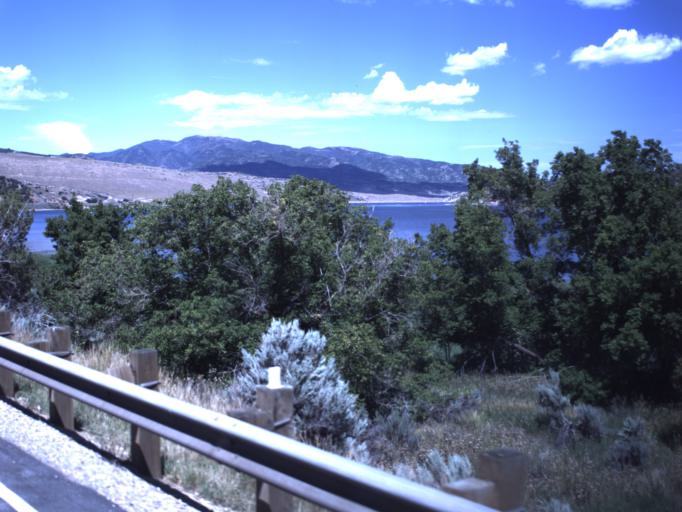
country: US
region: Utah
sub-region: Summit County
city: Oakley
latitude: 40.7553
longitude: -111.3841
